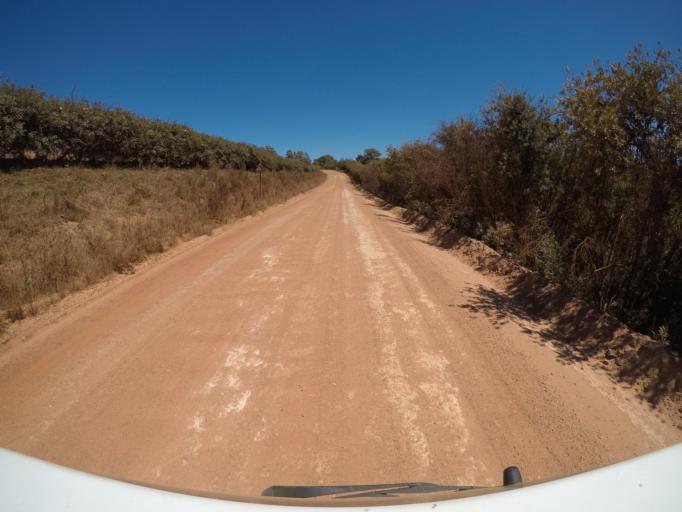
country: ZA
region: Western Cape
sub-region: Overberg District Municipality
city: Grabouw
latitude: -34.2376
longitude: 19.0807
